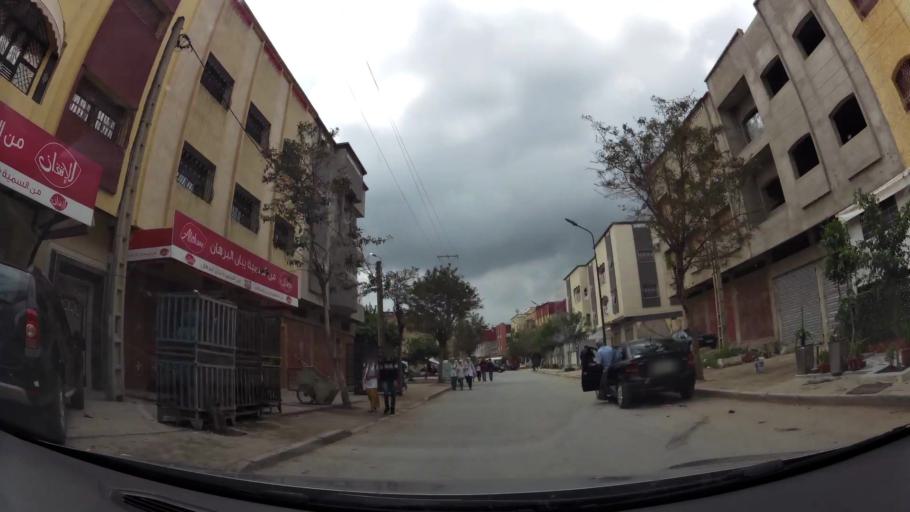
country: MA
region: Rabat-Sale-Zemmour-Zaer
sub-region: Khemisset
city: Tiflet
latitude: 33.8917
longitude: -6.3213
